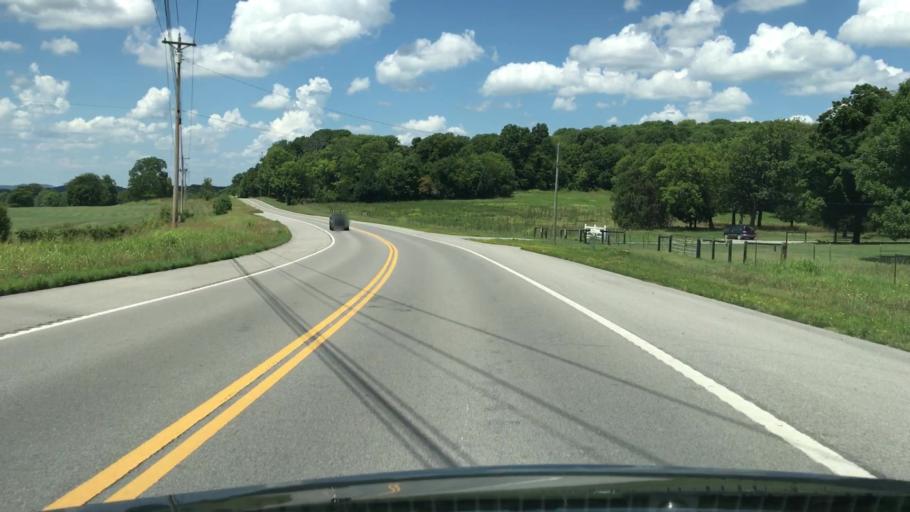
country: US
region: Tennessee
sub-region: Williamson County
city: Nolensville
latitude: 35.8511
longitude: -86.6179
